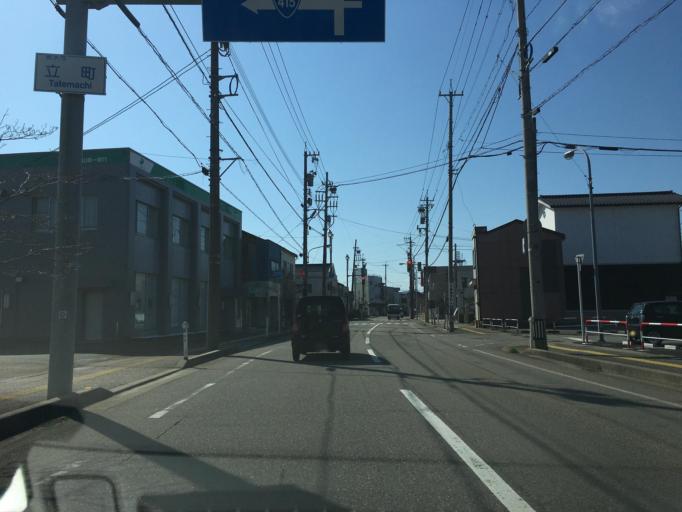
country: JP
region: Toyama
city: Nishishinminato
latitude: 36.7786
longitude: 137.0888
